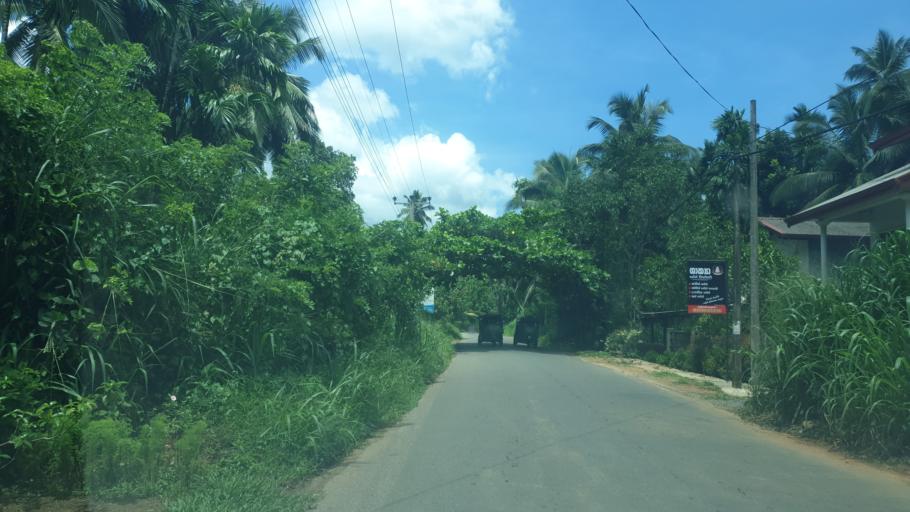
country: LK
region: Sabaragamuwa
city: Ratnapura
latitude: 6.4943
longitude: 80.3959
